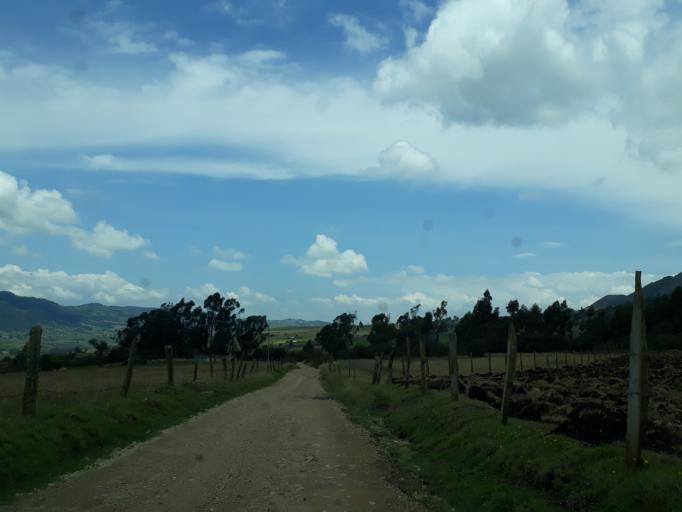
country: CO
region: Cundinamarca
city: Lenguazaque
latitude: 5.3154
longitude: -73.6279
